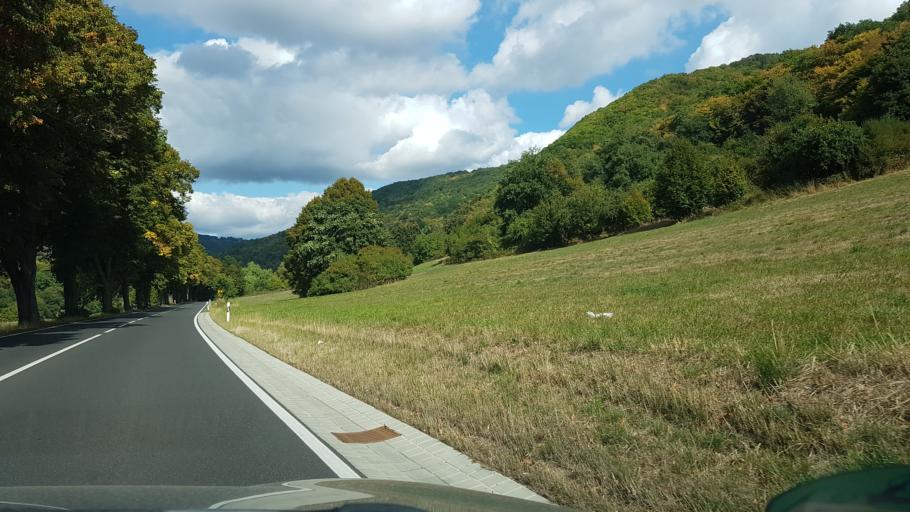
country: DE
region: Rheinland-Pfalz
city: Misselberg
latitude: 50.3164
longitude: 7.7683
